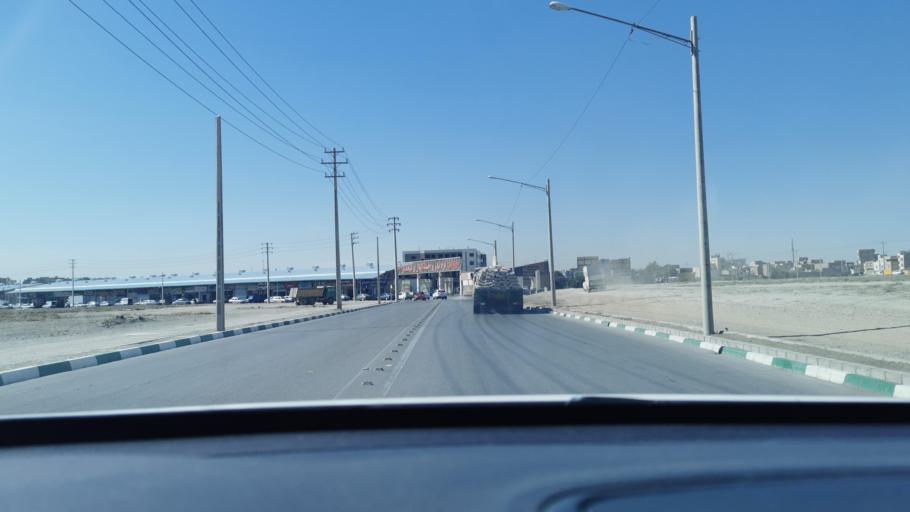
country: IR
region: Razavi Khorasan
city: Mashhad
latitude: 36.3361
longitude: 59.6214
